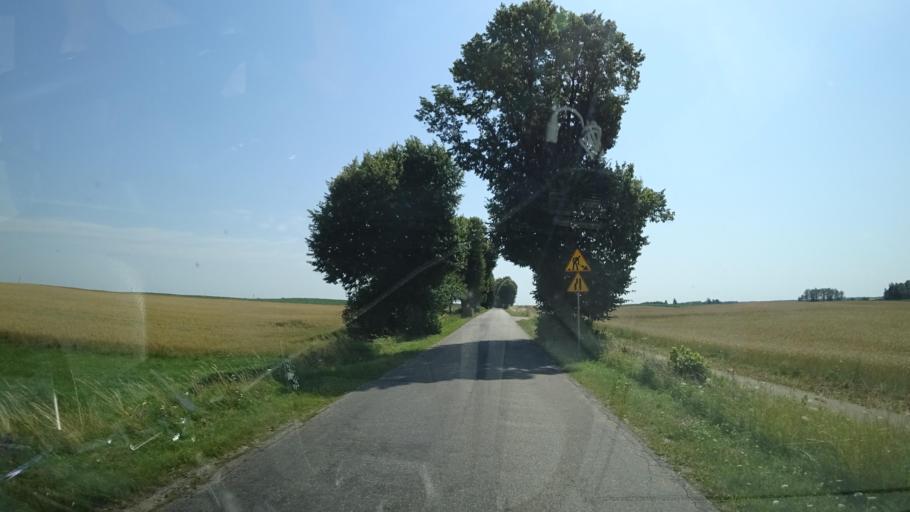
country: PL
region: Pomeranian Voivodeship
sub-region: Powiat chojnicki
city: Brusy
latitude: 53.8789
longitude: 17.6499
